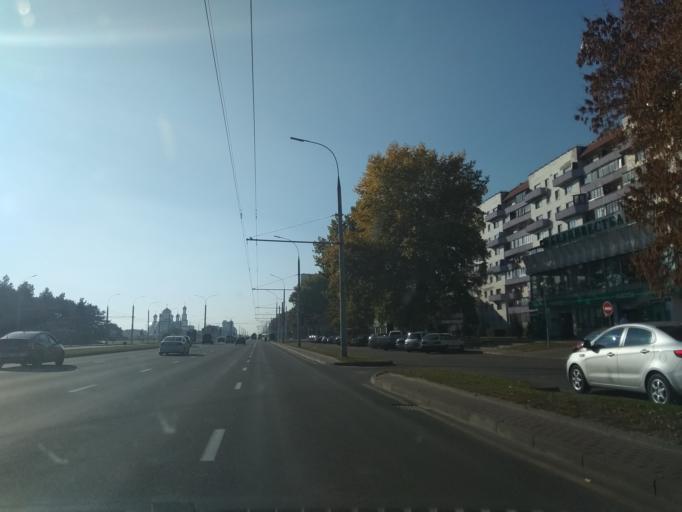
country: BY
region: Brest
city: Brest
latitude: 52.1016
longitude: 23.7731
